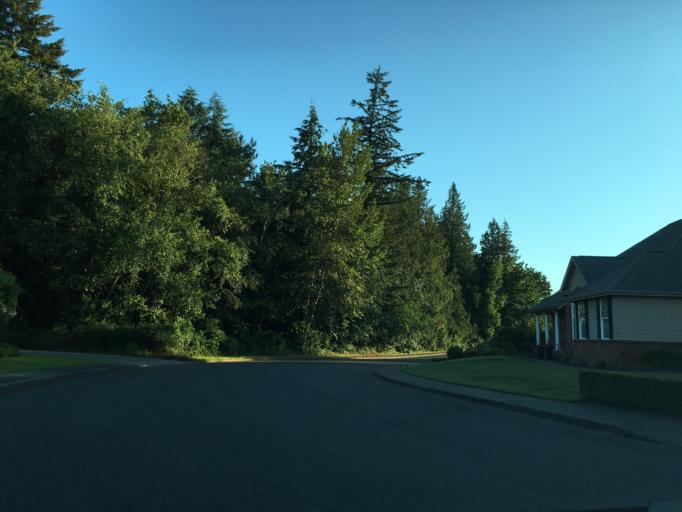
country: US
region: Washington
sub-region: Whatcom County
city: Lynden
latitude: 48.9562
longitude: -122.4269
